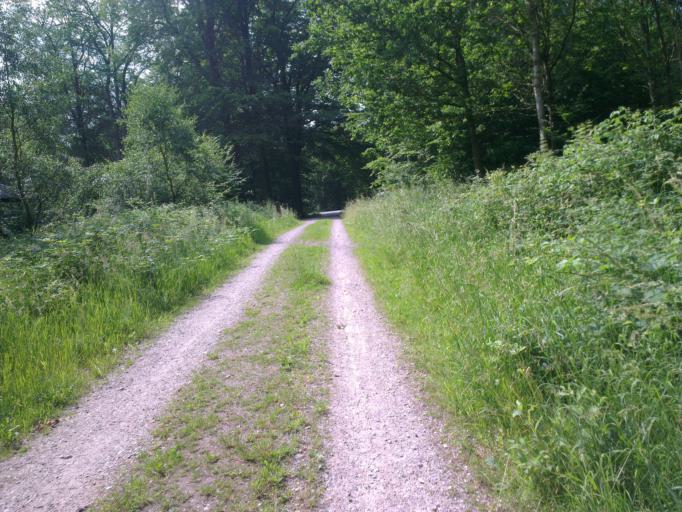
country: DK
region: Capital Region
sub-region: Allerod Kommune
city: Lillerod
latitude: 55.9035
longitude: 12.3567
